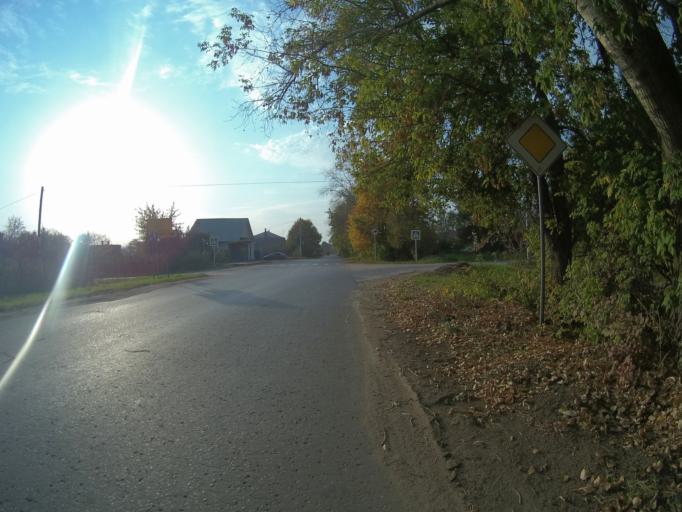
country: RU
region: Vladimir
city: Bogolyubovo
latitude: 56.1913
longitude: 40.4942
